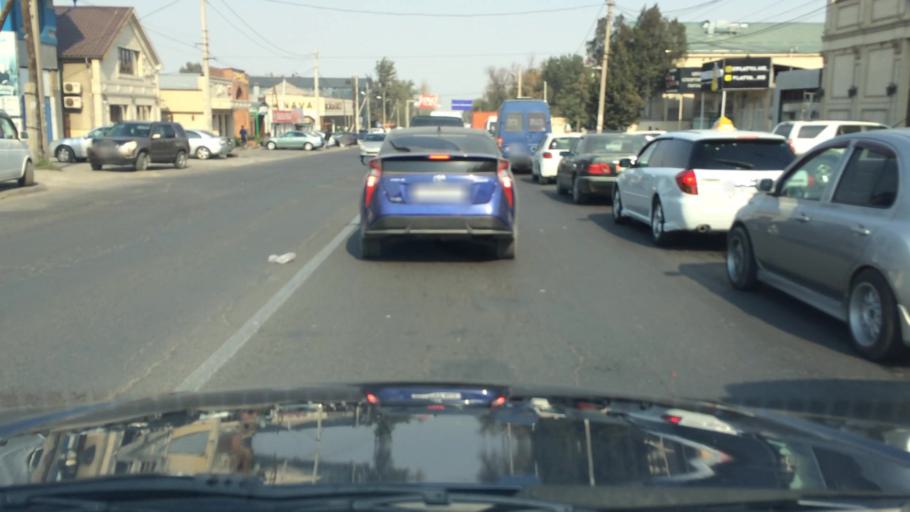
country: KG
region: Chuy
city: Lebedinovka
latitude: 42.8807
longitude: 74.6372
